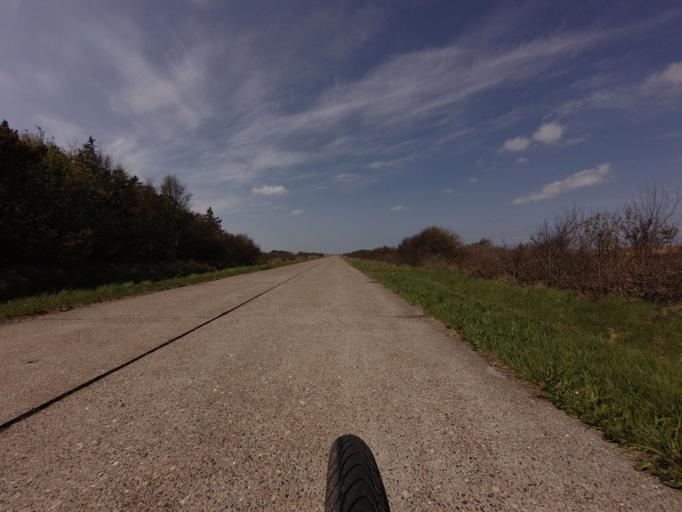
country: DK
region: North Denmark
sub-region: Jammerbugt Kommune
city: Brovst
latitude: 57.1722
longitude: 9.4593
